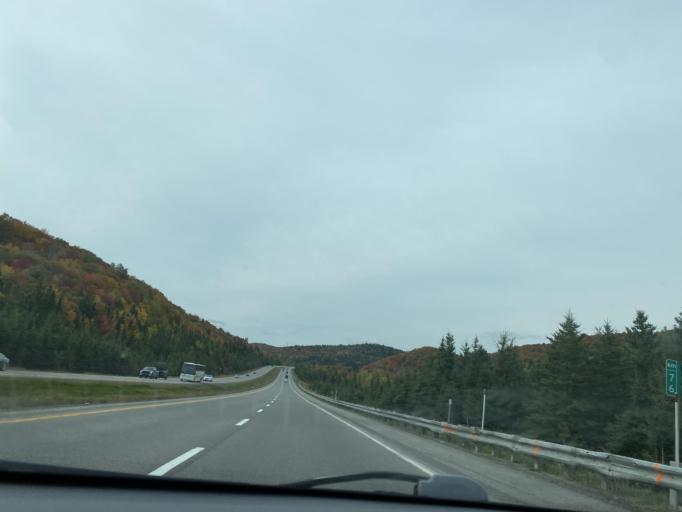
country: CA
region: Quebec
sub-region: Laurentides
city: Val-David
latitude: 45.9903
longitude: -74.2005
